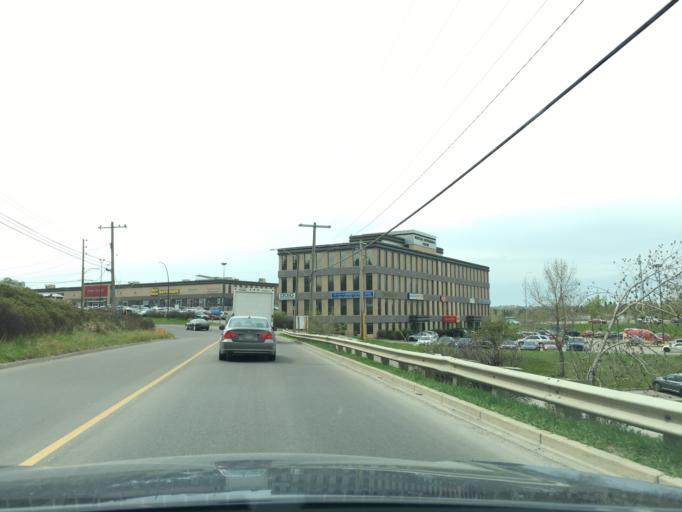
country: CA
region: Alberta
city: Calgary
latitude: 50.9827
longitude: -114.0693
